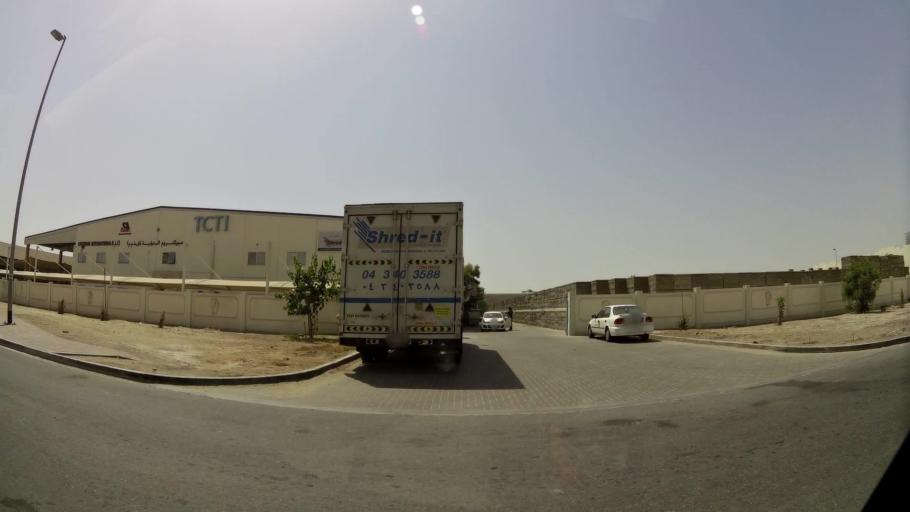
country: AE
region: Dubai
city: Dubai
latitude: 25.1475
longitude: 55.2407
